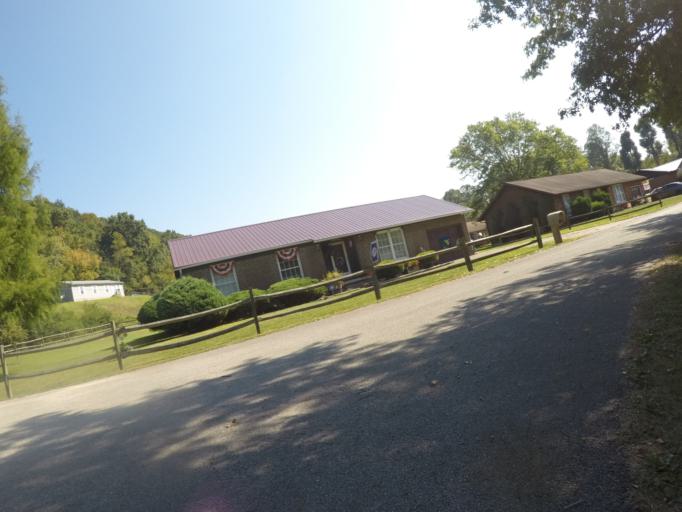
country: US
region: West Virginia
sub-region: Cabell County
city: Barboursville
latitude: 38.3704
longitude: -82.2726
